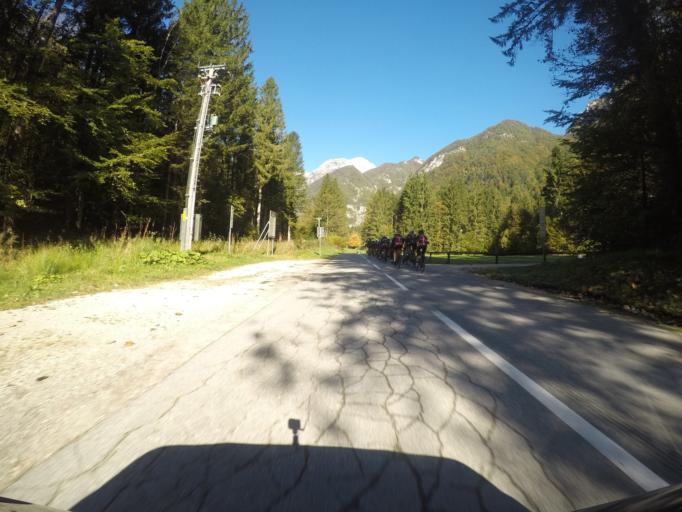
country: SI
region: Kamnik
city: Mekinje
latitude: 46.3101
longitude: 14.6077
